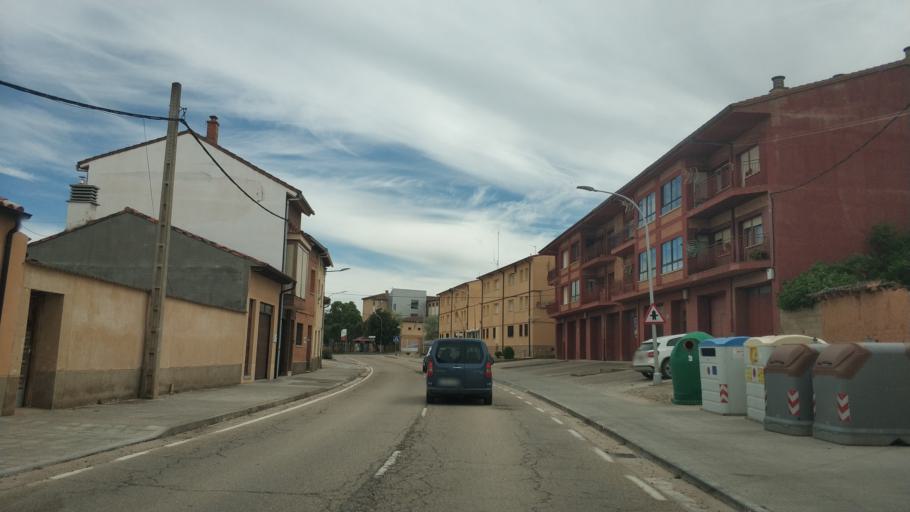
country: ES
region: Castille and Leon
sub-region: Provincia de Soria
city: Berlanga de Duero
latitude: 41.4659
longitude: -2.8630
